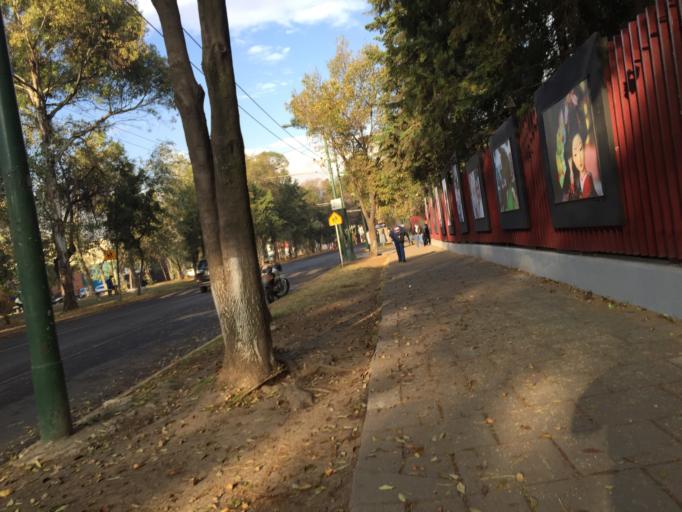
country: MX
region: Mexico
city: Colonia Lindavista
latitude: 19.4959
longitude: -99.1389
